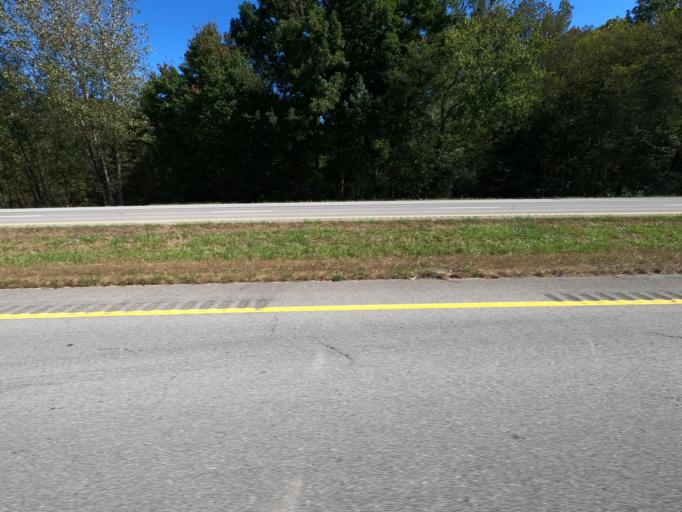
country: US
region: Tennessee
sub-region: Maury County
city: Mount Pleasant
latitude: 35.4167
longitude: -87.2821
